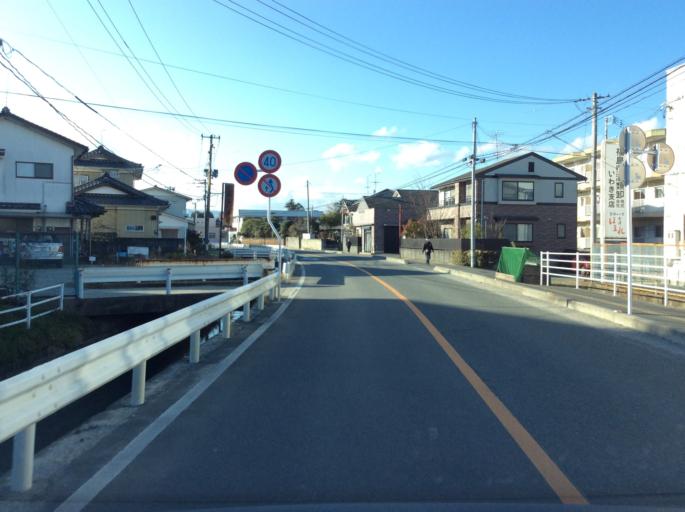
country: JP
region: Fukushima
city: Iwaki
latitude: 37.0522
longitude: 140.9133
